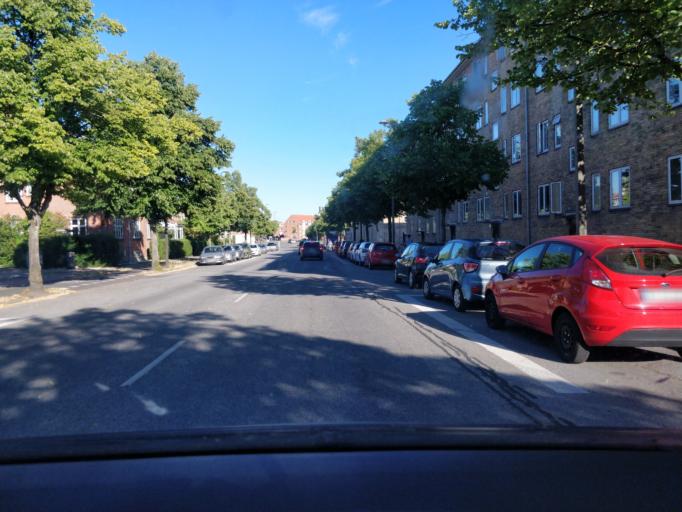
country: DK
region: Capital Region
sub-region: Kobenhavn
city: Vanlose
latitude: 55.6949
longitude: 12.4914
